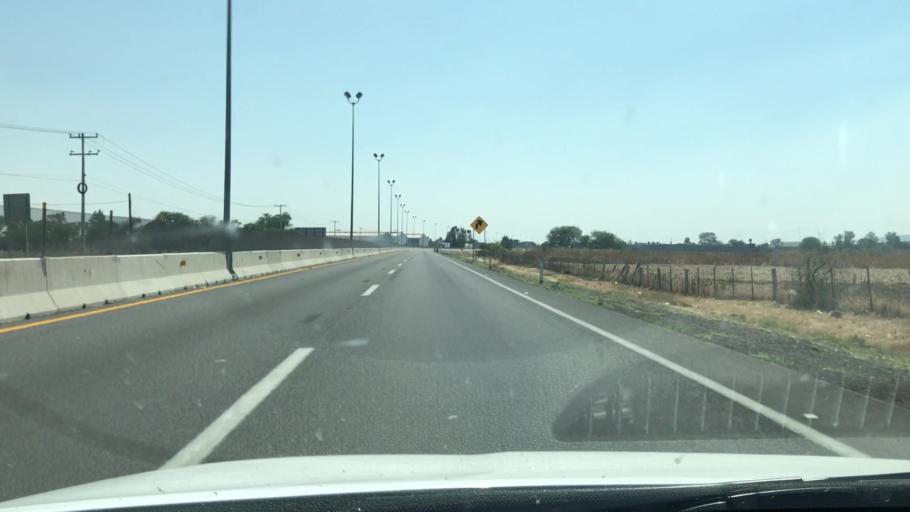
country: MX
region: Guanajuato
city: Abasolo
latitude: 20.4630
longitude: -101.5213
